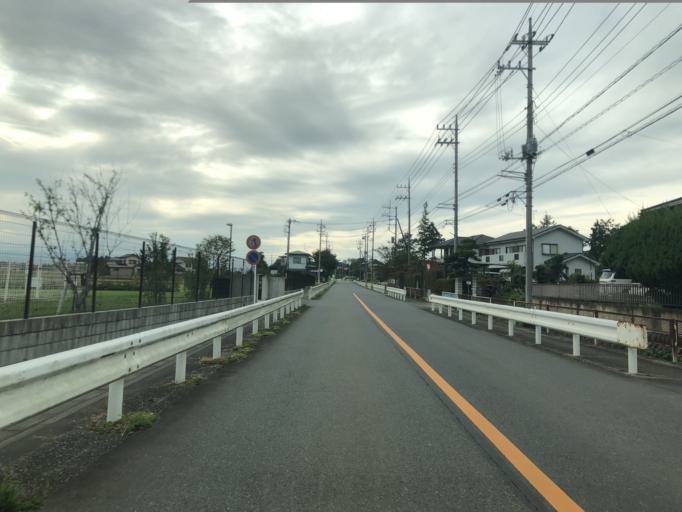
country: JP
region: Saitama
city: Fukiage-fujimi
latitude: 36.0614
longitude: 139.3956
